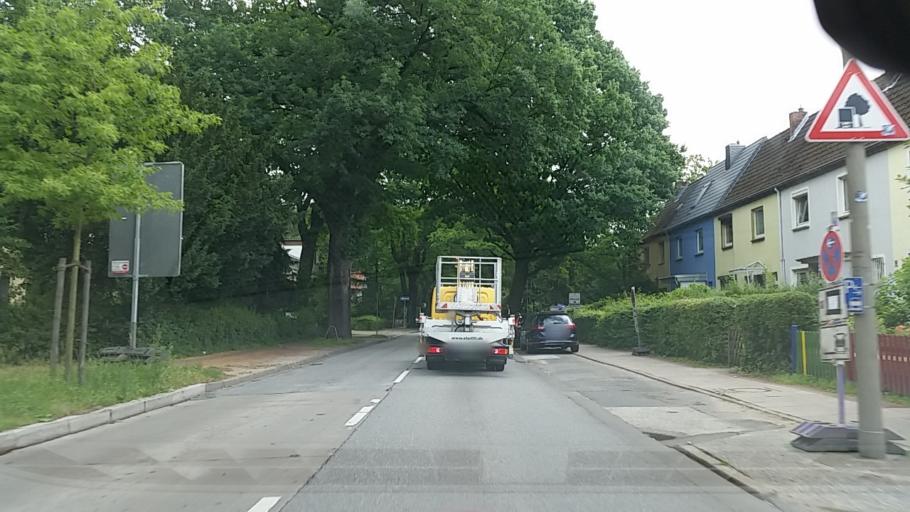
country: DE
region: Hamburg
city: Eidelstedt
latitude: 53.6337
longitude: 9.9128
